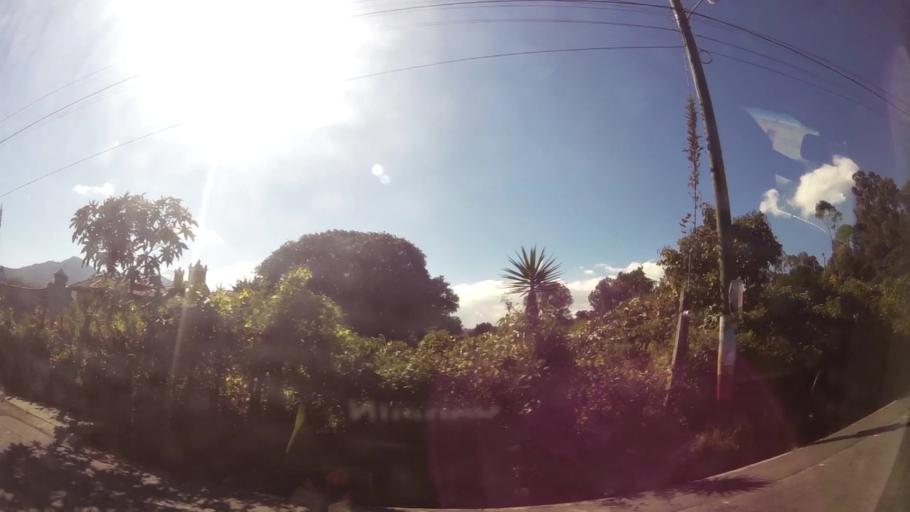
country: GT
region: Sacatepequez
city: Santa Lucia Milpas Altas
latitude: 14.5689
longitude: -90.6394
